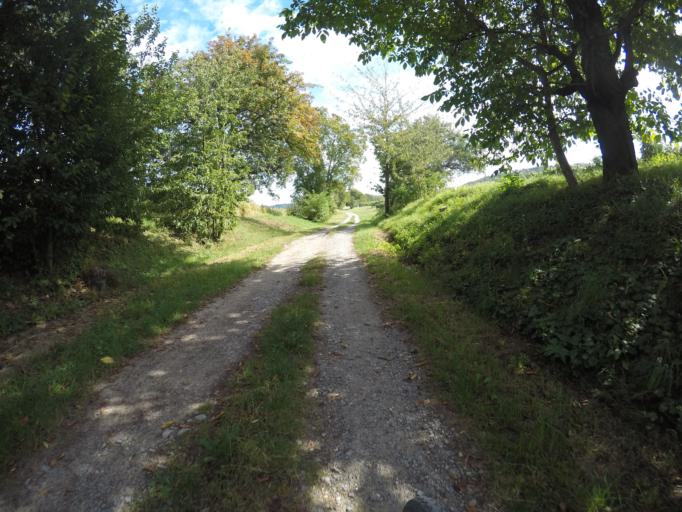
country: DE
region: Baden-Wuerttemberg
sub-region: Karlsruhe Region
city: Kurnbach
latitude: 49.0699
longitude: 8.8337
